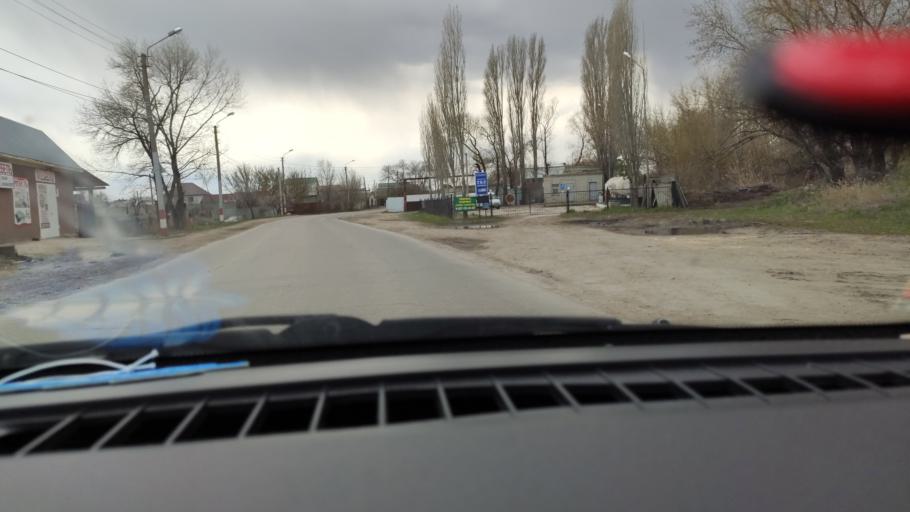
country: RU
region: Saratov
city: Engel's
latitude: 51.4993
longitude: 46.0627
